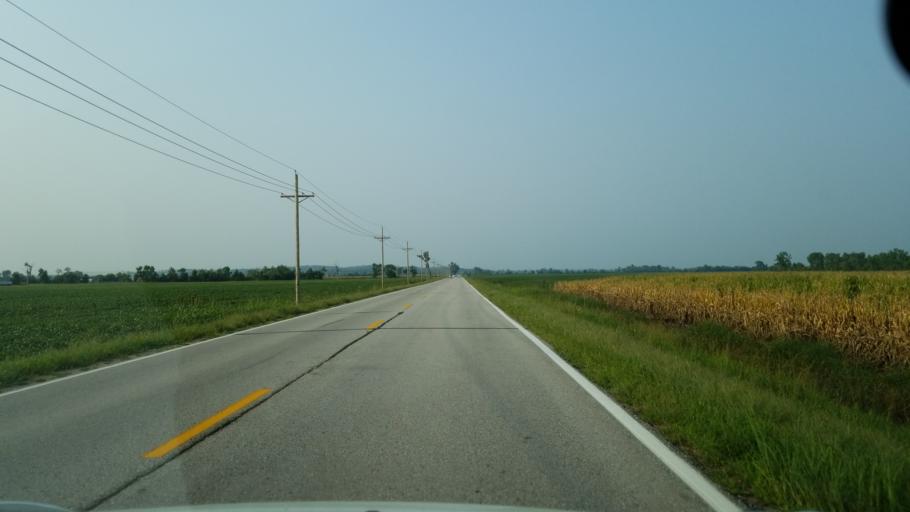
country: US
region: Nebraska
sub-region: Sarpy County
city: Offutt Air Force Base
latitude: 41.0920
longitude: -95.8898
